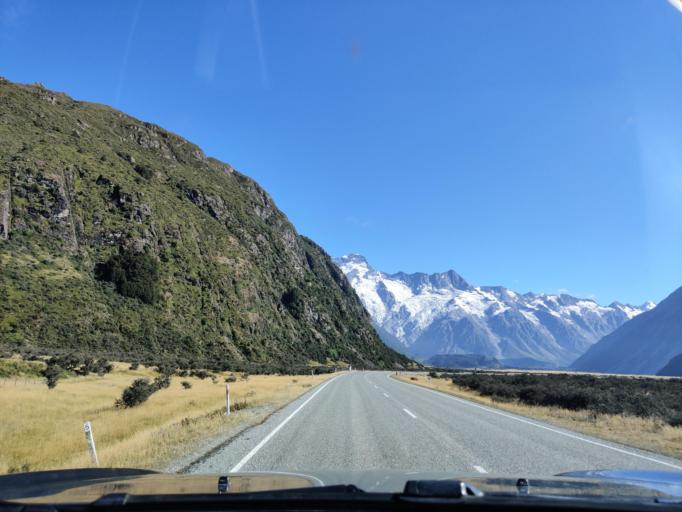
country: NZ
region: Canterbury
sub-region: Timaru District
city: Pleasant Point
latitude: -43.7584
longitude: 170.1187
